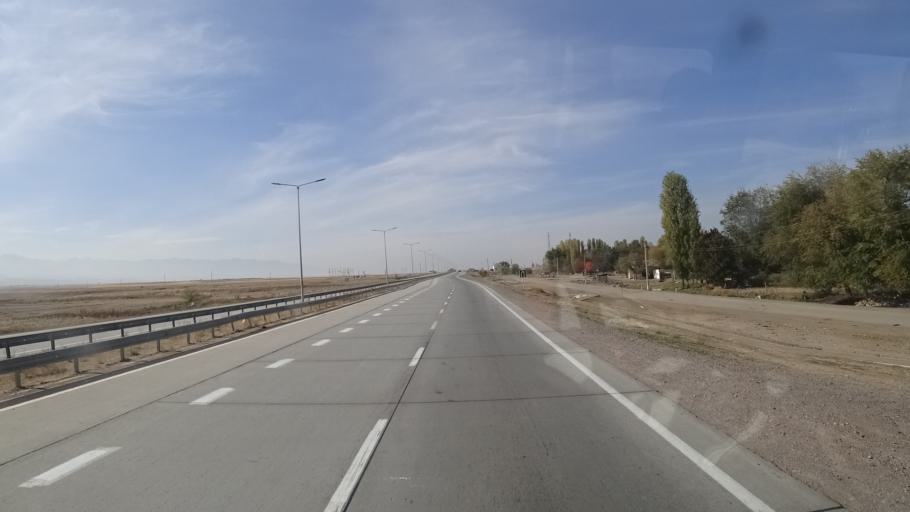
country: KZ
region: Zhambyl
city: Merke
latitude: 42.8887
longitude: 72.9936
